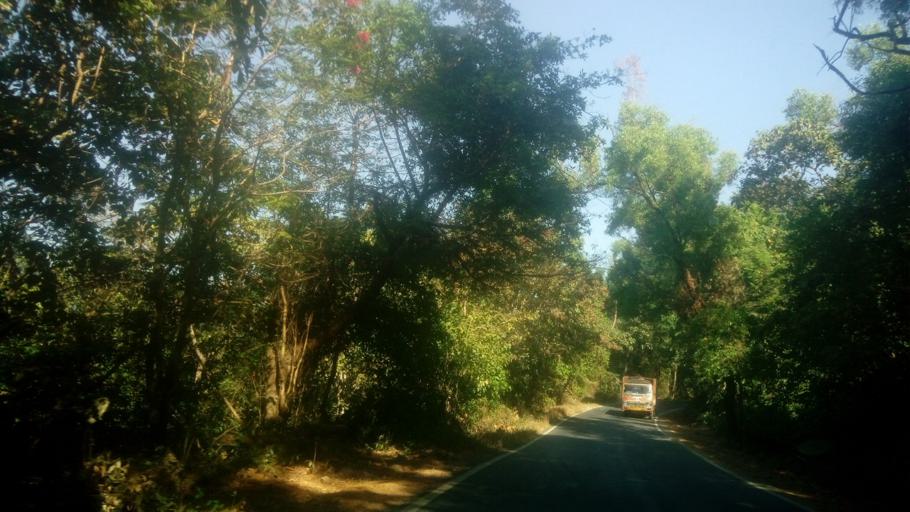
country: IN
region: Goa
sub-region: North Goa
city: Valpoy
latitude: 15.6119
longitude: 74.1126
